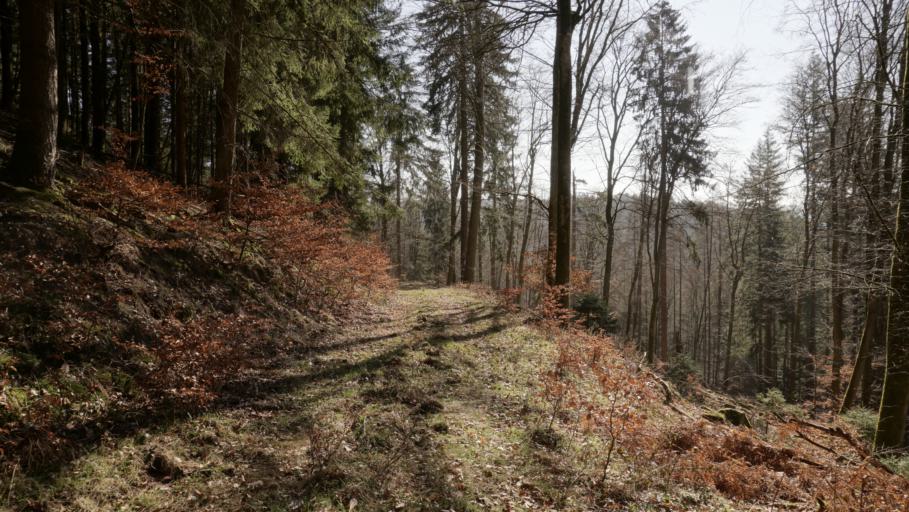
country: DE
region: Baden-Wuerttemberg
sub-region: Karlsruhe Region
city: Neckargerach
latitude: 49.4230
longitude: 9.0986
